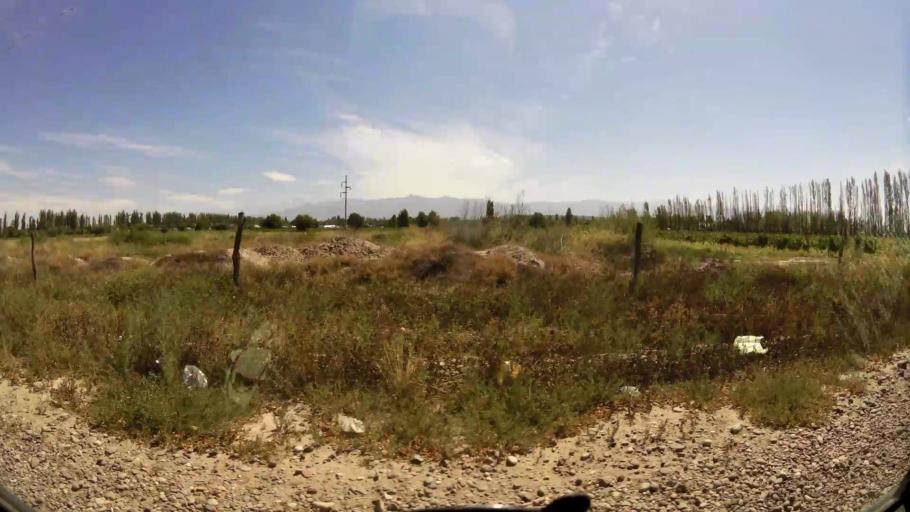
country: AR
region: Mendoza
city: Lujan de Cuyo
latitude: -32.9877
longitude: -68.8513
